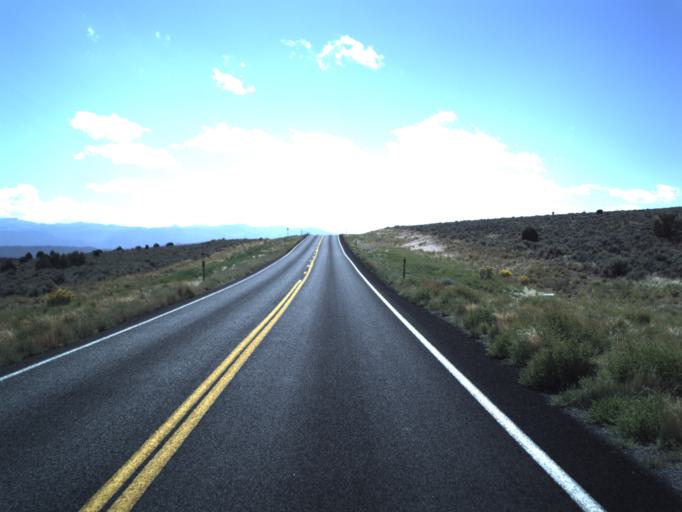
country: US
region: Utah
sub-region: Iron County
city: Parowan
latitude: 38.0317
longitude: -112.9984
